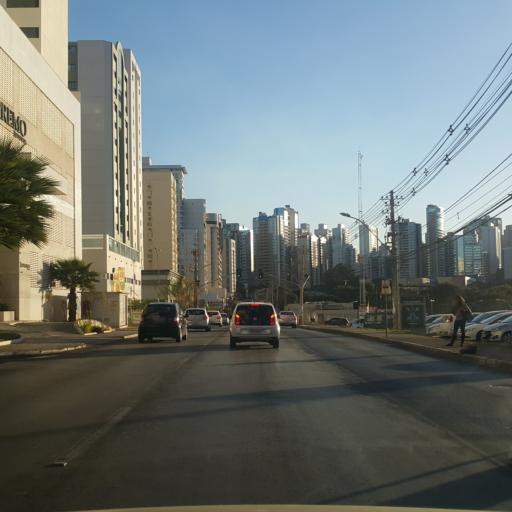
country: BR
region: Federal District
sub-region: Brasilia
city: Brasilia
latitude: -15.8364
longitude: -48.0203
